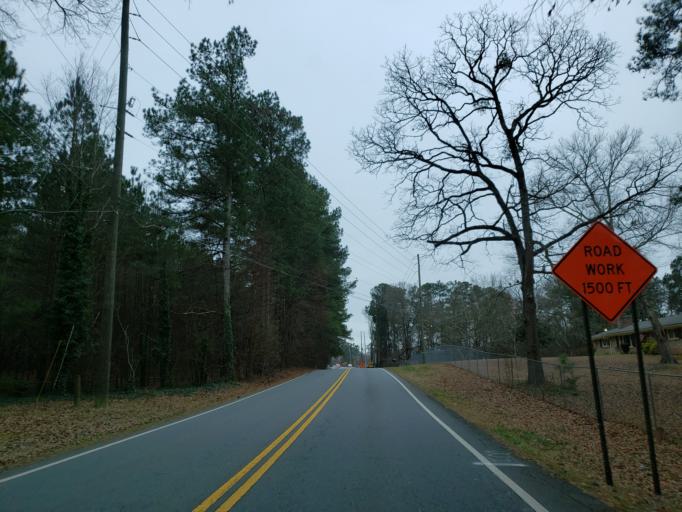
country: US
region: Georgia
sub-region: Cobb County
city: Powder Springs
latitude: 33.9049
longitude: -84.6669
